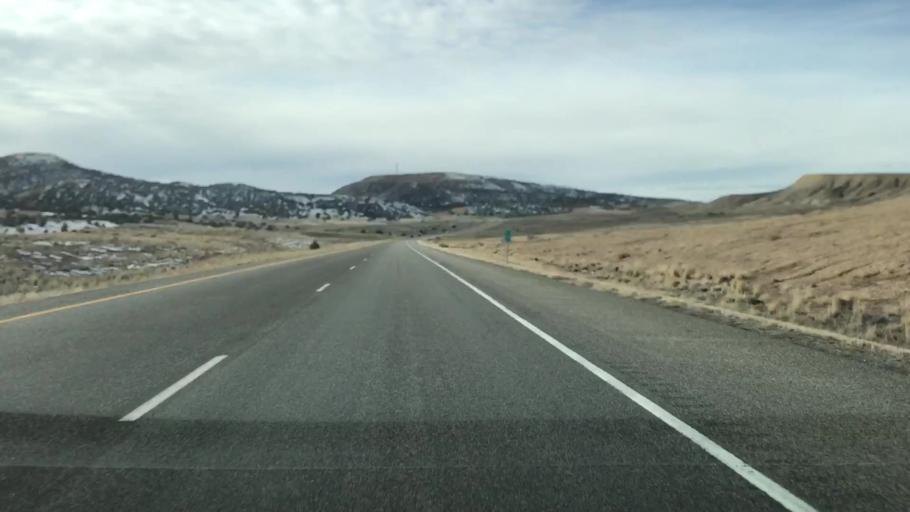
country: US
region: Colorado
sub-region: Mesa County
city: Loma
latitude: 39.2249
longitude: -108.9371
